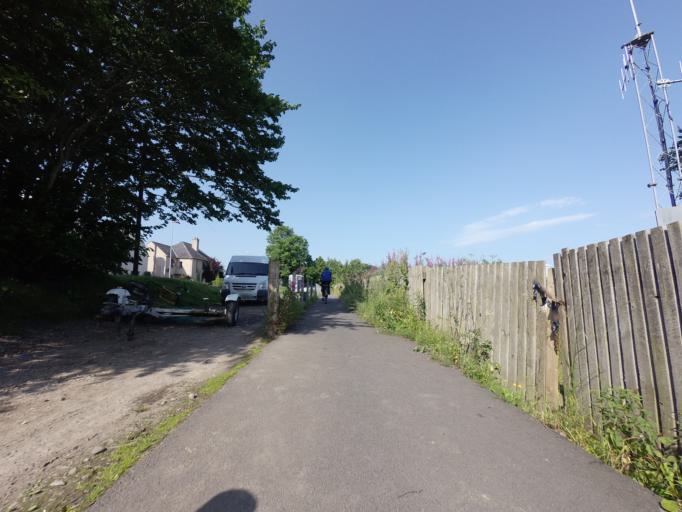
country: GB
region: Scotland
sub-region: Highland
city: Evanton
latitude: 57.6682
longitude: -4.3259
